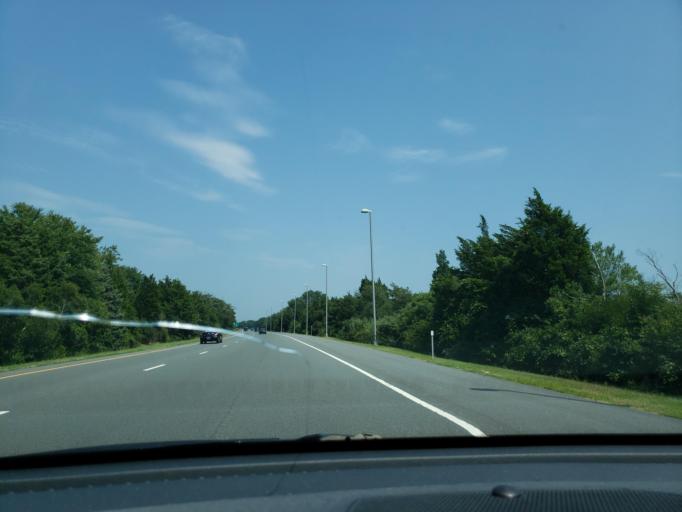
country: US
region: New Jersey
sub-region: Cape May County
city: Sea Isle City
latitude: 39.1965
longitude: -74.7063
